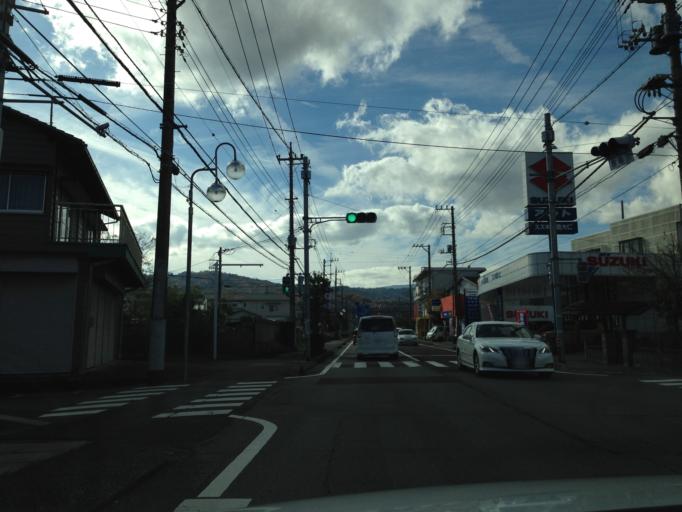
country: JP
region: Shizuoka
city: Mishima
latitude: 34.9985
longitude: 138.9379
